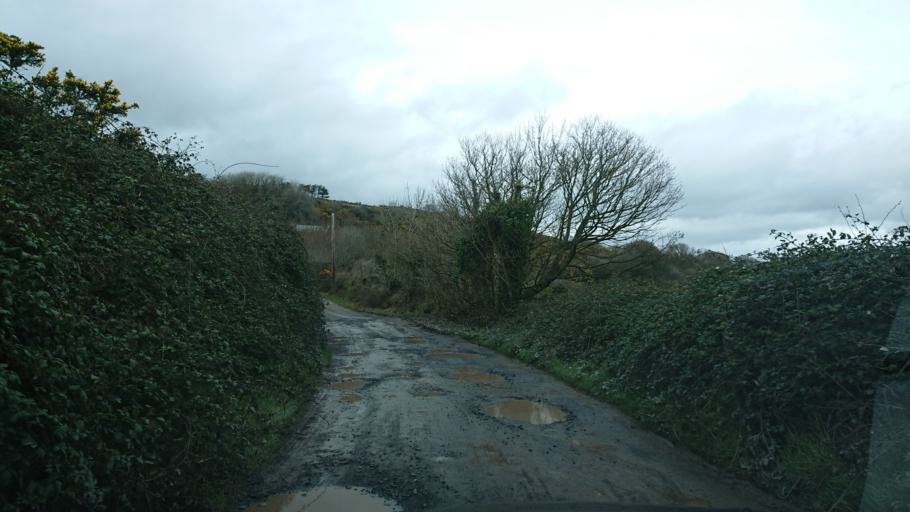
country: IE
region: Munster
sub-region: Waterford
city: Dunmore East
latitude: 52.1810
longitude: -6.9899
